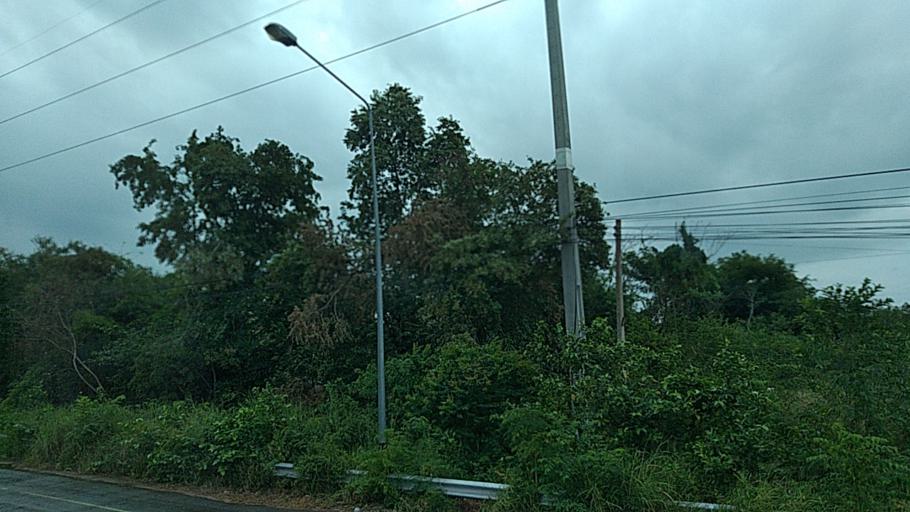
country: TH
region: Maha Sarakham
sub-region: Amphoe Borabue
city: Borabue
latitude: 16.0421
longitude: 103.1274
